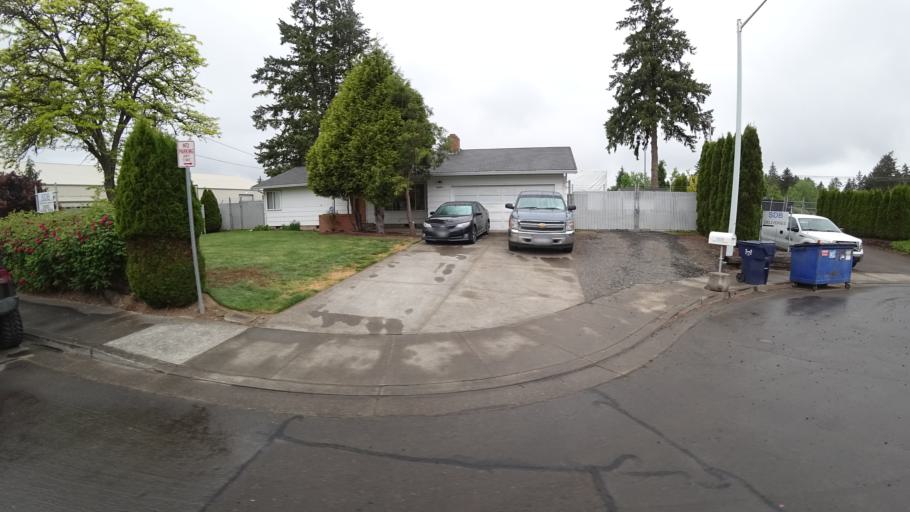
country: US
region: Oregon
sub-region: Washington County
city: Rockcreek
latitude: 45.5304
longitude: -122.8958
